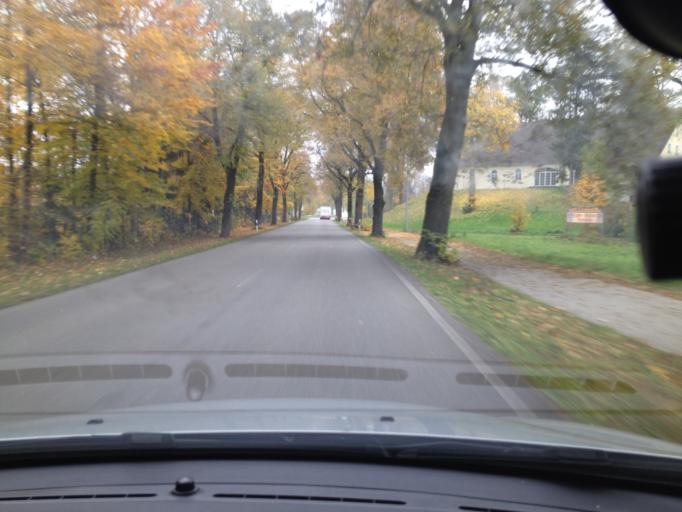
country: DE
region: Bavaria
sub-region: Swabia
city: Ettringen
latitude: 48.1096
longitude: 10.6688
